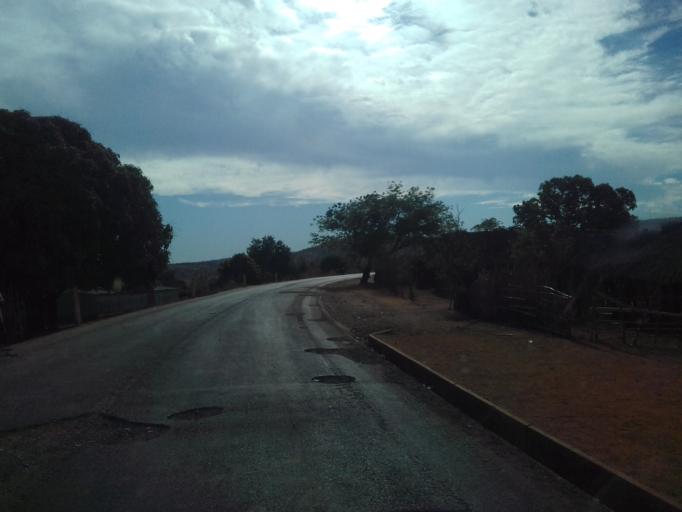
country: MG
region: Sofia
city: Antsohihy
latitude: -15.3810
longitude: 47.7052
